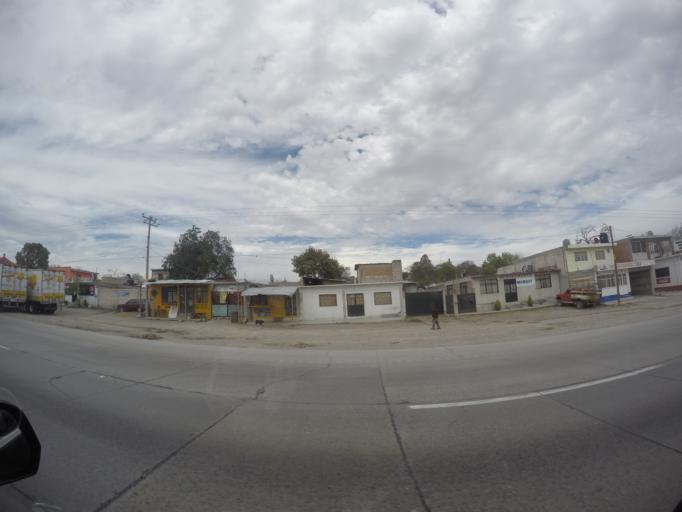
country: MX
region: Queretaro
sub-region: San Juan del Rio
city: Paso de Mata
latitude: 20.3413
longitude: -99.9448
